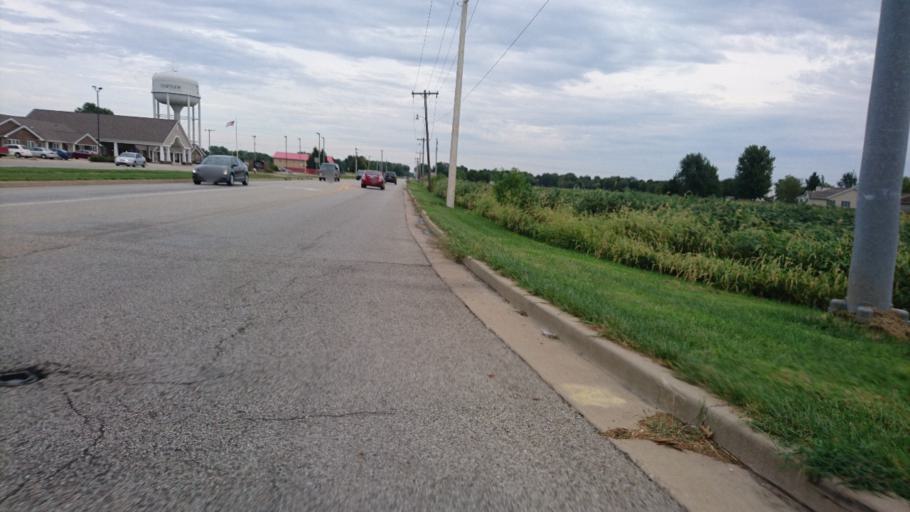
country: US
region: Illinois
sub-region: Sangamon County
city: Chatham
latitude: 39.6766
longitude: -89.6954
